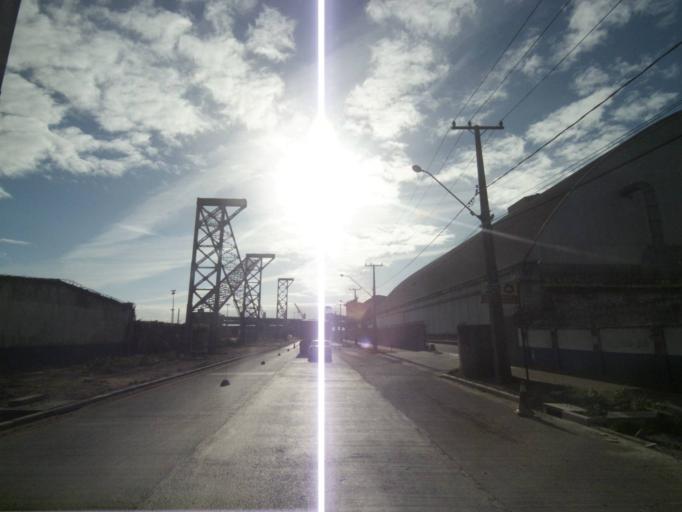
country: BR
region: Parana
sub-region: Paranagua
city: Paranagua
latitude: -25.5051
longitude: -48.5245
